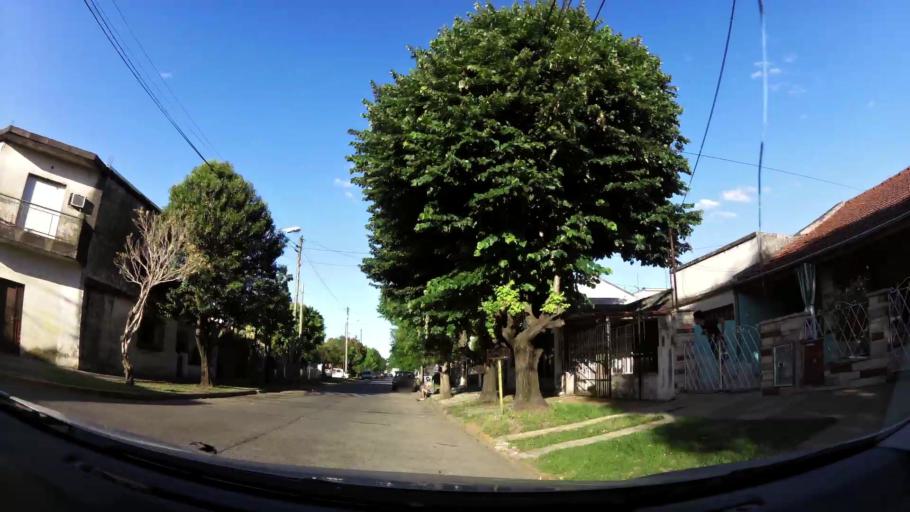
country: AR
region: Buenos Aires
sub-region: Partido de Tigre
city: Tigre
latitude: -34.4623
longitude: -58.5665
